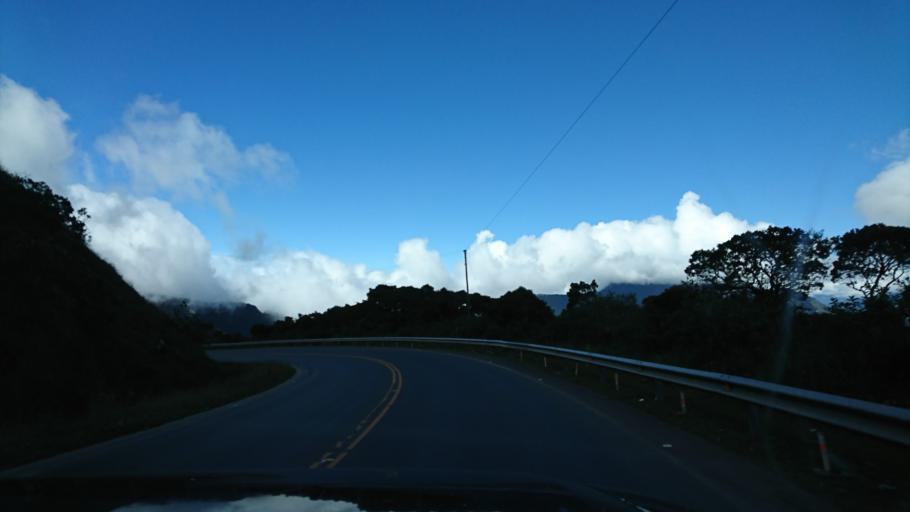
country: BO
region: La Paz
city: Coroico
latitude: -16.2924
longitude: -67.8564
